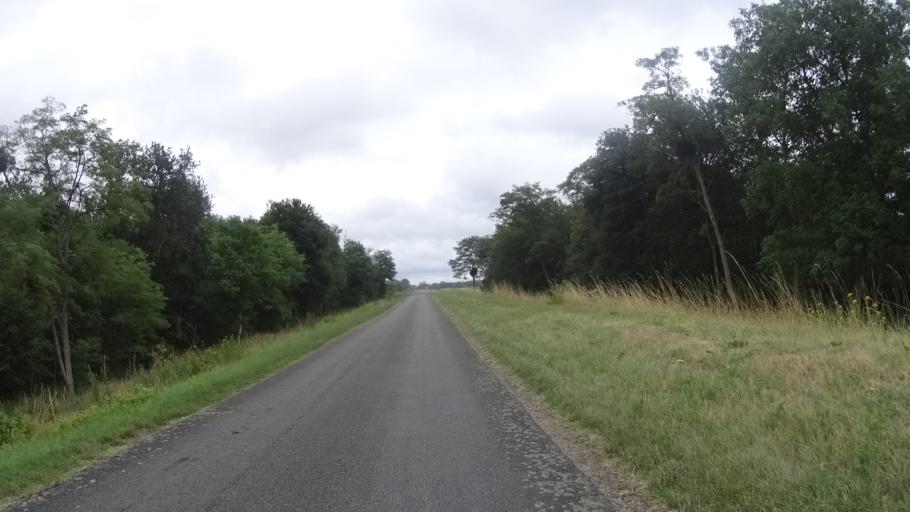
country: FR
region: Centre
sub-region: Departement du Loir-et-Cher
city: Suevres
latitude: 47.6574
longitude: 1.4613
